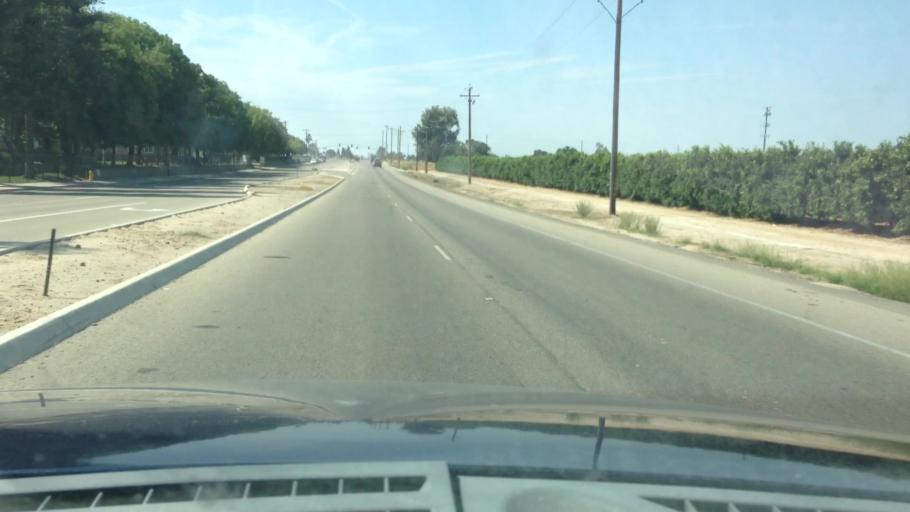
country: US
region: California
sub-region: Fresno County
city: Parlier
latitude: 36.6095
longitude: -119.5568
